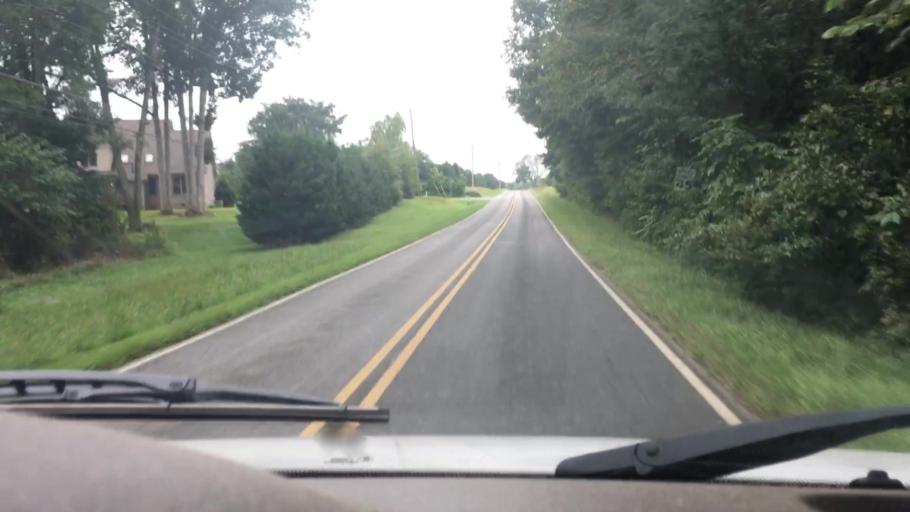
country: US
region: North Carolina
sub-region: Gaston County
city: Davidson
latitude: 35.5175
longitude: -80.8231
